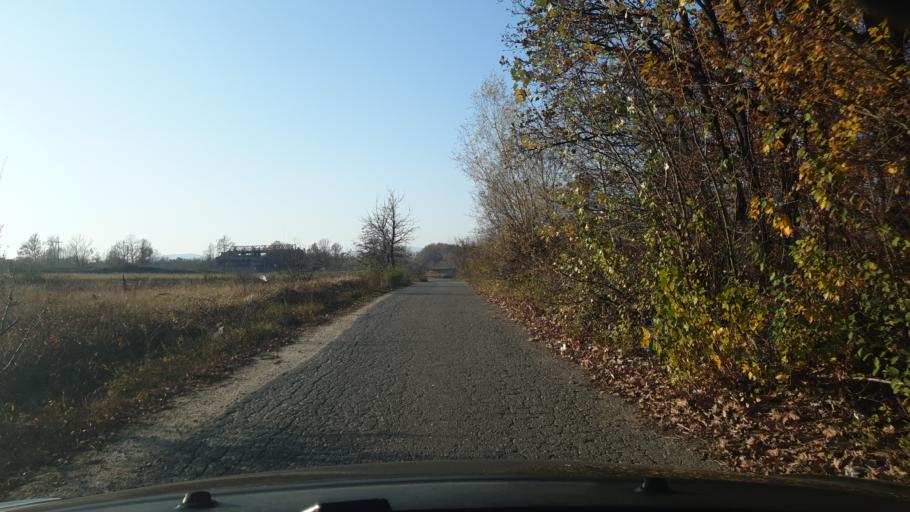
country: RS
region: Central Serbia
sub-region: Borski Okrug
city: Negotin
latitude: 44.1470
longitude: 22.3569
